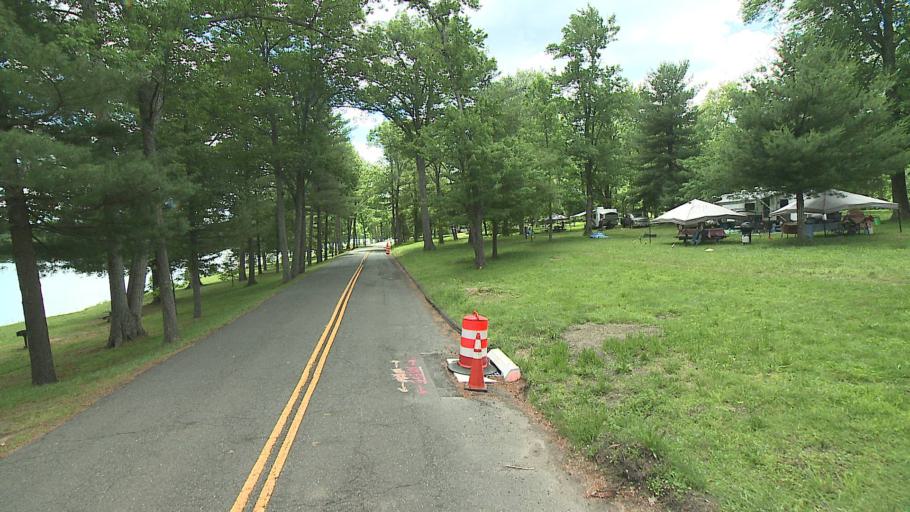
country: US
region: Connecticut
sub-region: Litchfield County
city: New Preston
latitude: 41.7060
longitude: -73.3822
